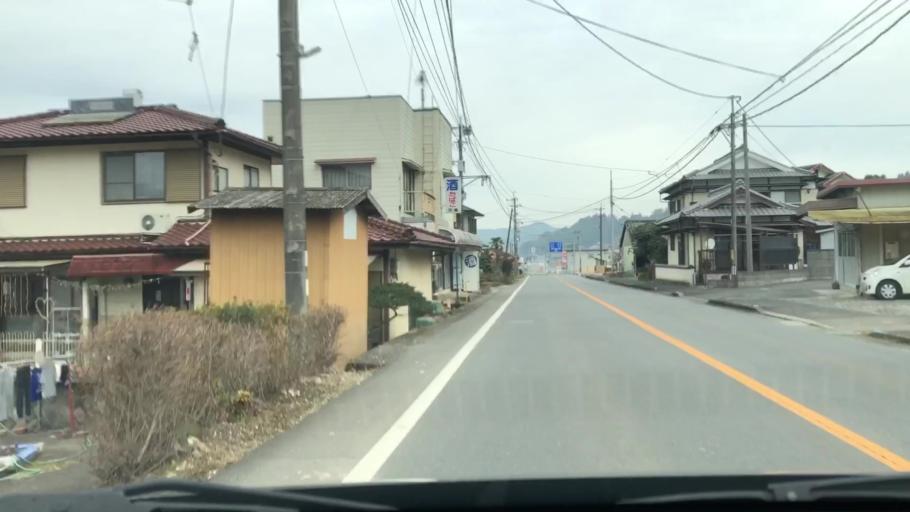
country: JP
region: Oita
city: Usuki
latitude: 33.0298
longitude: 131.6879
